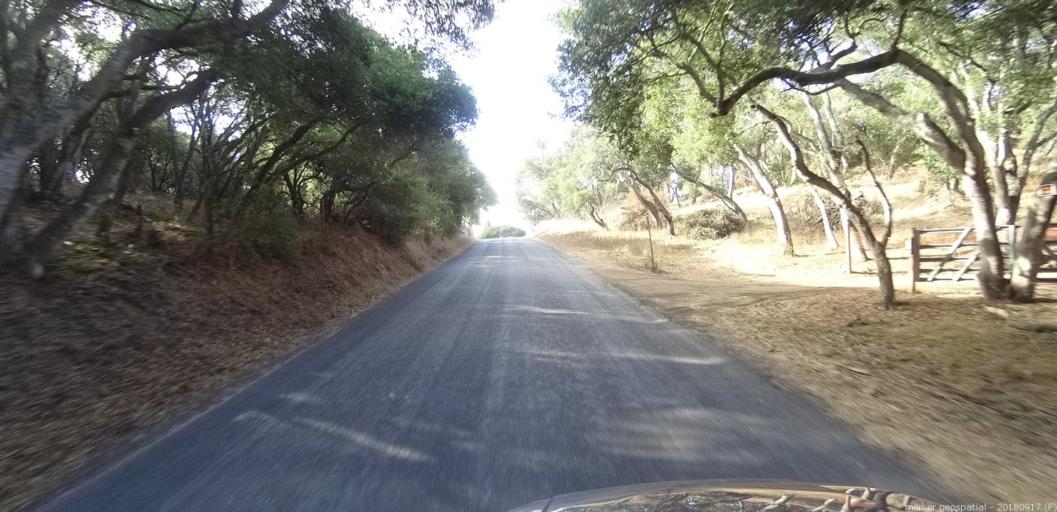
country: US
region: California
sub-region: Monterey County
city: Elkhorn
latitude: 36.8087
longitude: -121.7136
